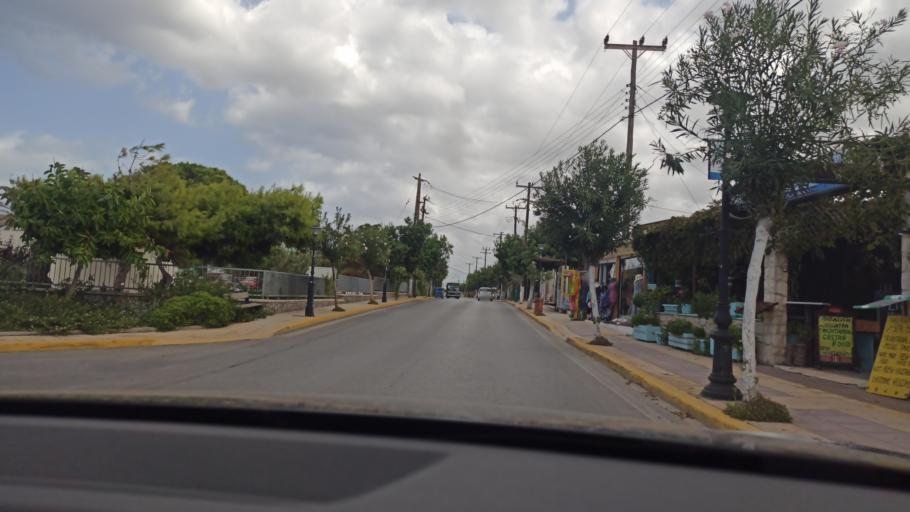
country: GR
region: Crete
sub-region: Nomos Irakleiou
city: Gazi
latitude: 35.3358
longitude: 25.0804
